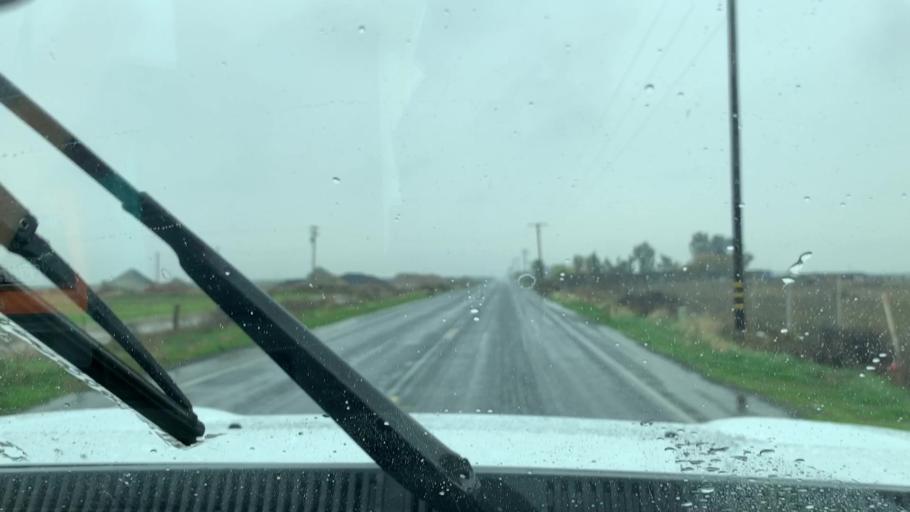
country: US
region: California
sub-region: Tulare County
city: Earlimart
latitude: 35.8919
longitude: -119.3115
